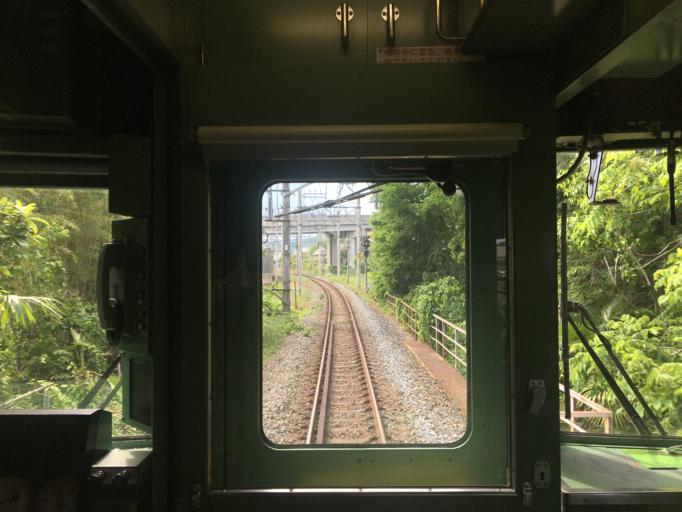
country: JP
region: Saitama
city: Yorii
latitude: 36.1177
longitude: 139.1989
